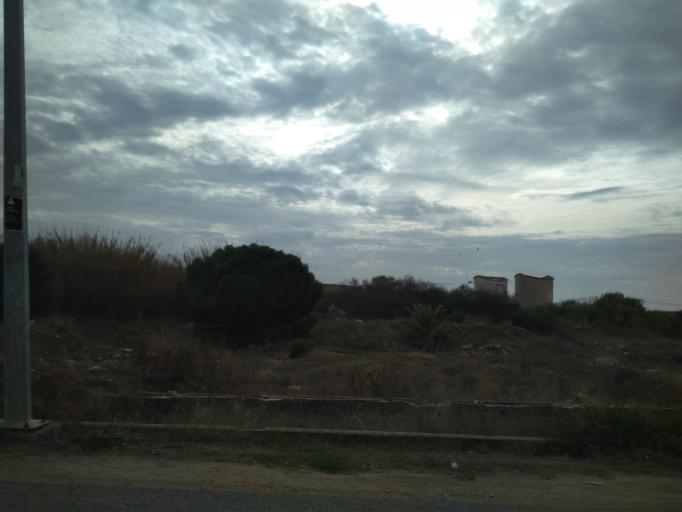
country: PT
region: Faro
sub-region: Faro
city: Faro
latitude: 37.0260
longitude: -7.8964
